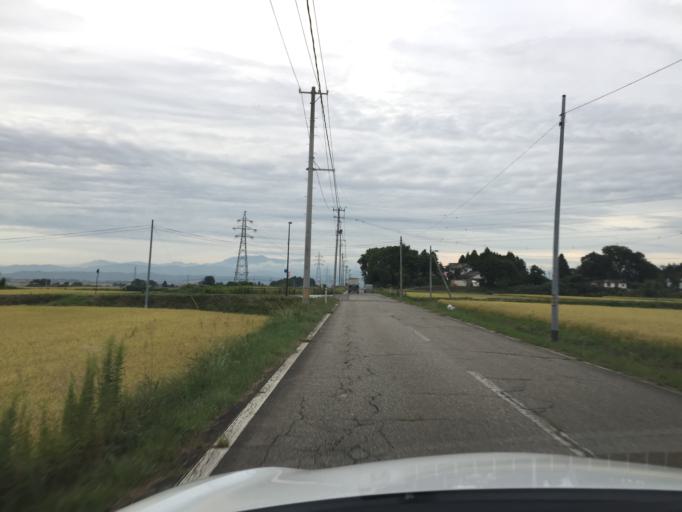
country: JP
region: Fukushima
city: Kitakata
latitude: 37.5583
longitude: 139.9332
